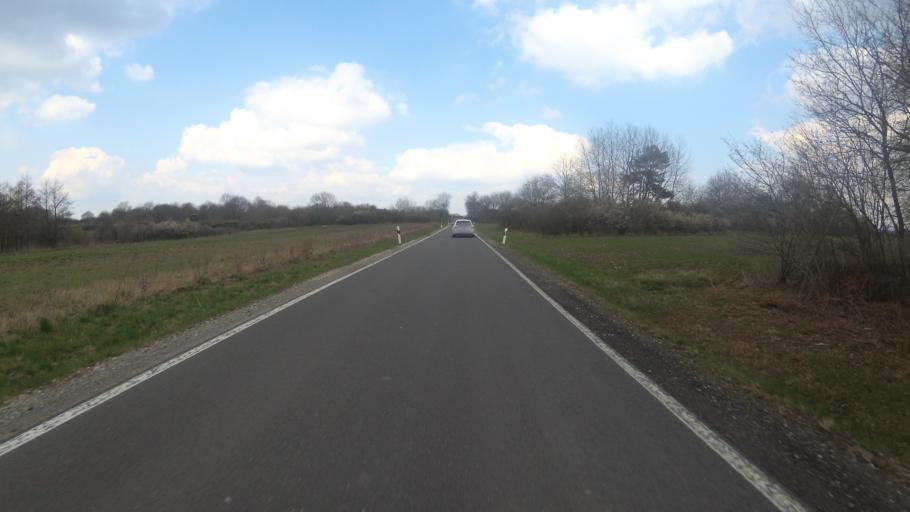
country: DE
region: Rheinland-Pfalz
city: Polich
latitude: 49.7683
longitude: 6.8478
